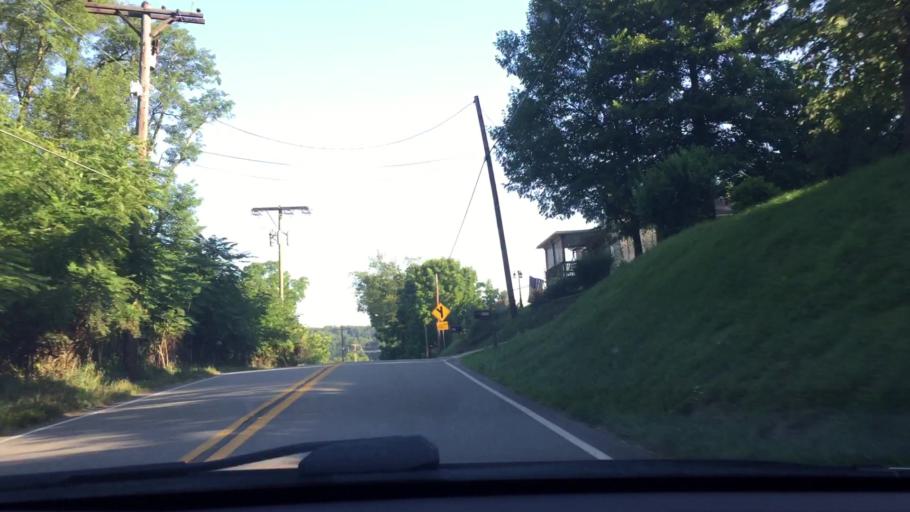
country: US
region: Pennsylvania
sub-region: Washington County
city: East Washington
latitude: 40.1976
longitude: -80.2214
